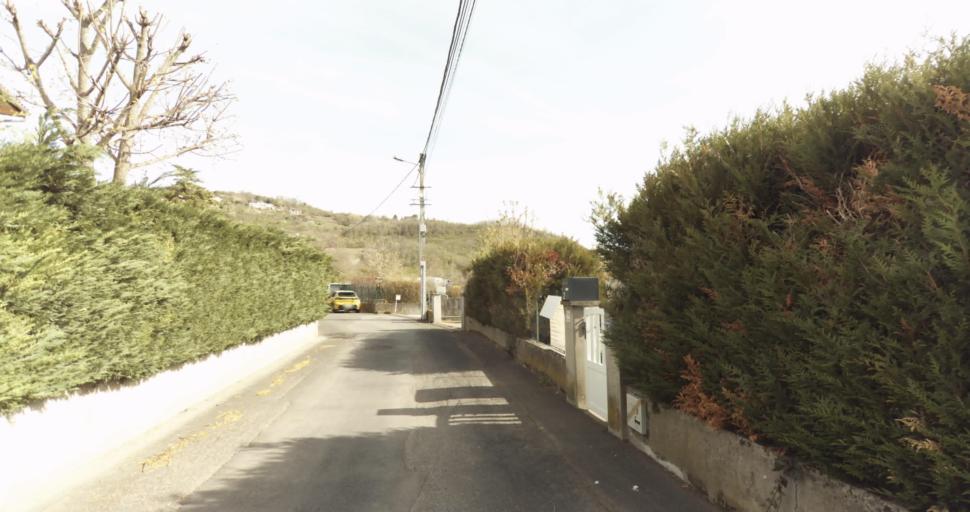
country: FR
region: Auvergne
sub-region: Departement du Puy-de-Dome
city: Blanzat
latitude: 45.8352
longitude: 3.0813
